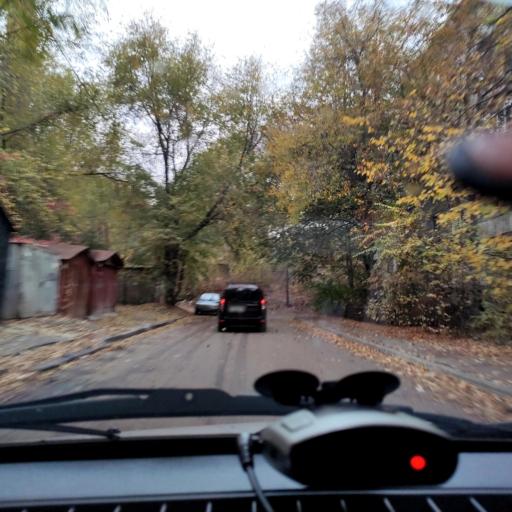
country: RU
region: Voronezj
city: Voronezh
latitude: 51.6456
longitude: 39.1628
